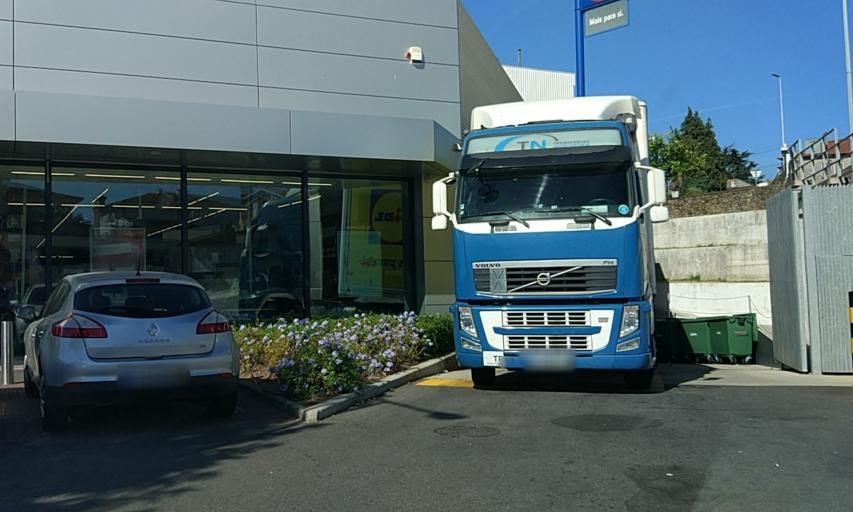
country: PT
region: Porto
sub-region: Santo Tirso
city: Santo Tirso
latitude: 41.3453
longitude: -8.4826
